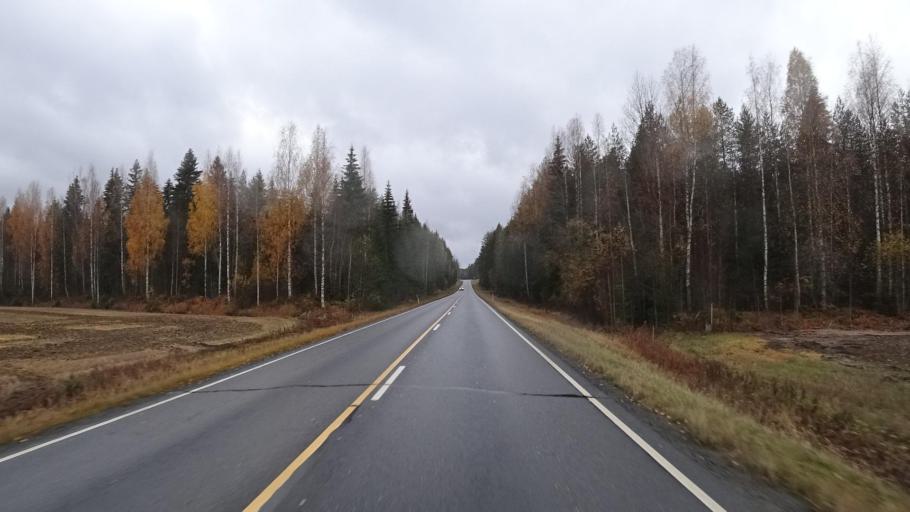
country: FI
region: Southern Savonia
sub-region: Mikkeli
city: Kangasniemi
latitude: 62.1638
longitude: 26.8391
